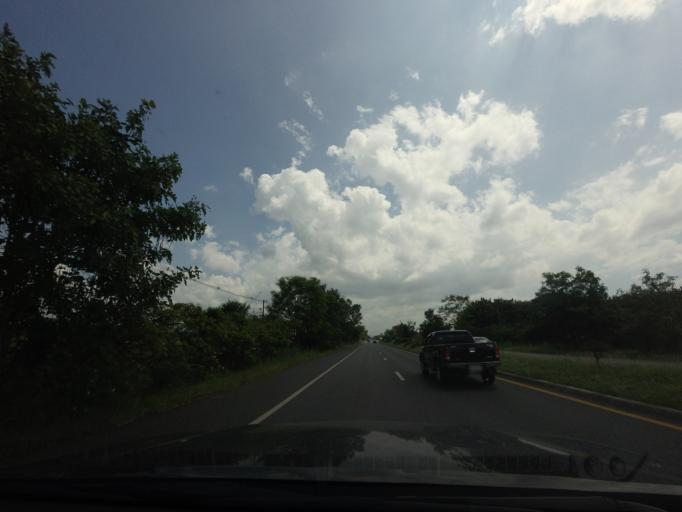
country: TH
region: Phetchabun
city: Phetchabun
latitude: 16.2385
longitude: 101.0787
